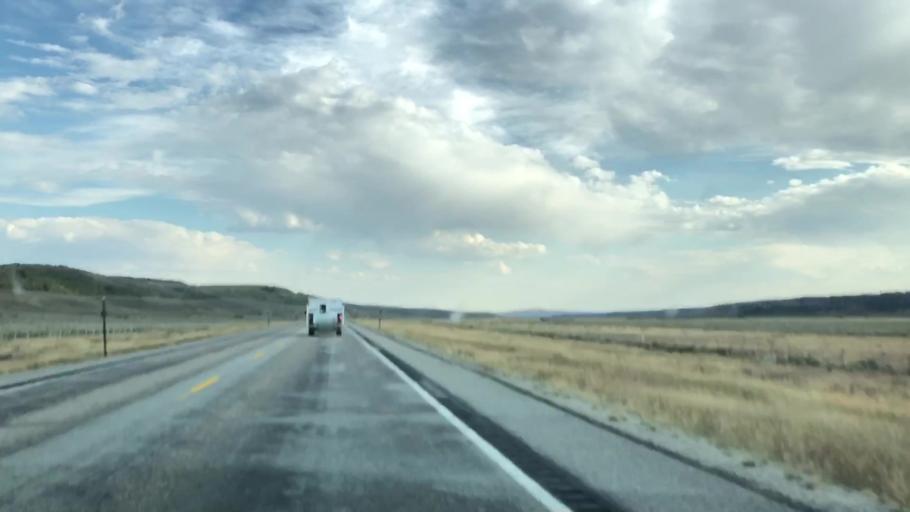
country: US
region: Wyoming
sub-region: Sublette County
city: Pinedale
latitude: 43.1051
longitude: -110.1712
